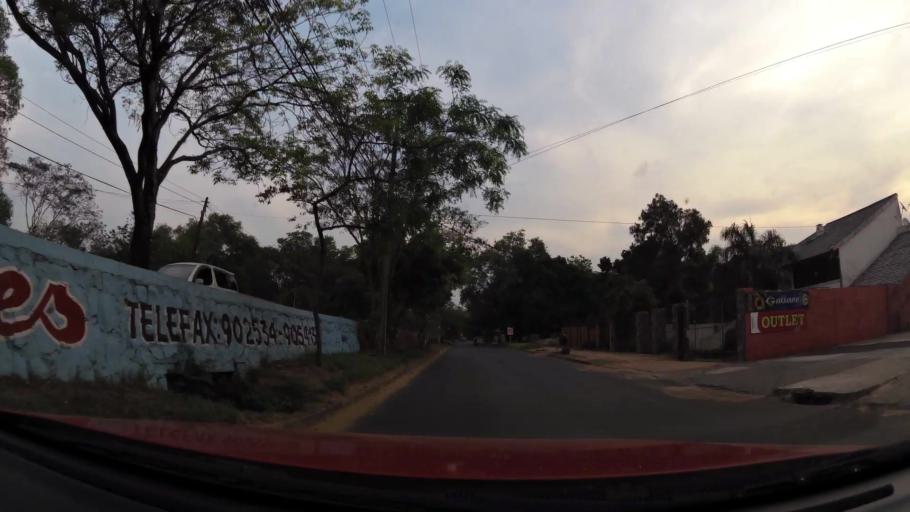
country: PY
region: Central
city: Lambare
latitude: -25.3456
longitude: -57.6390
